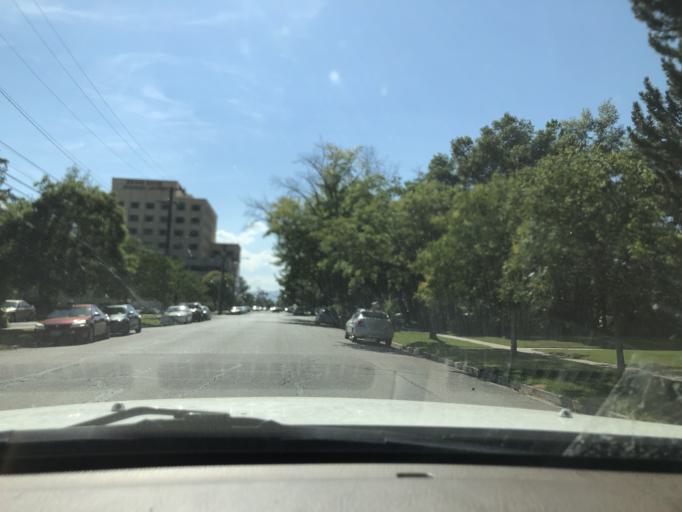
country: US
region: Utah
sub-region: Utah County
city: Provo
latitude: 40.2365
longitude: -111.6559
